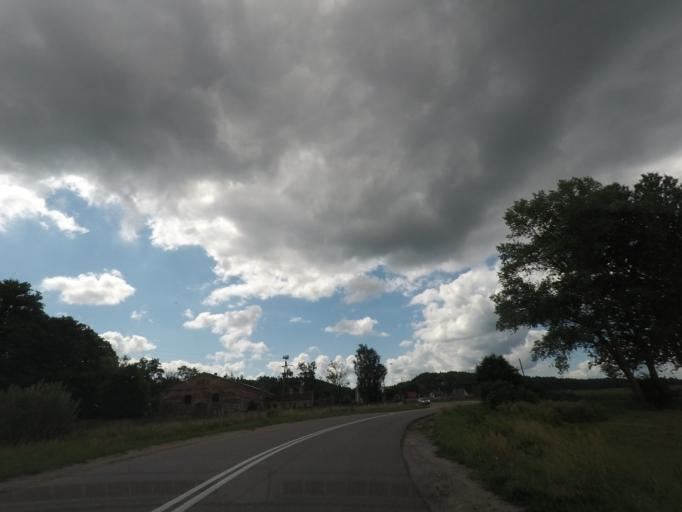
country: PL
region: Pomeranian Voivodeship
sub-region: Powiat wejherowski
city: Leczyce
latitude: 54.5765
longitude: 17.8657
